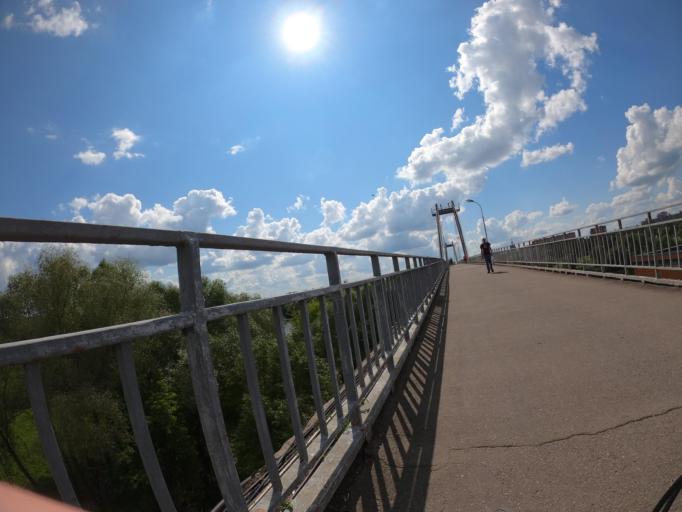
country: RU
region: Moskovskaya
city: Voskresensk
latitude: 55.3189
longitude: 38.6662
